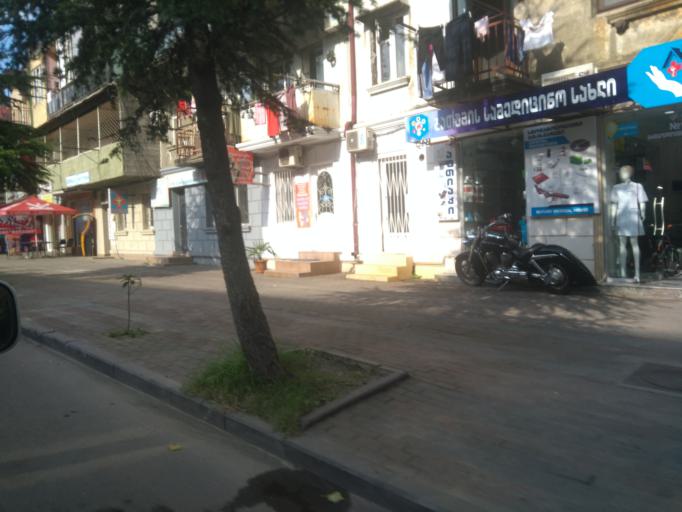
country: GE
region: Ajaria
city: Batumi
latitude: 41.6403
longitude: 41.6252
